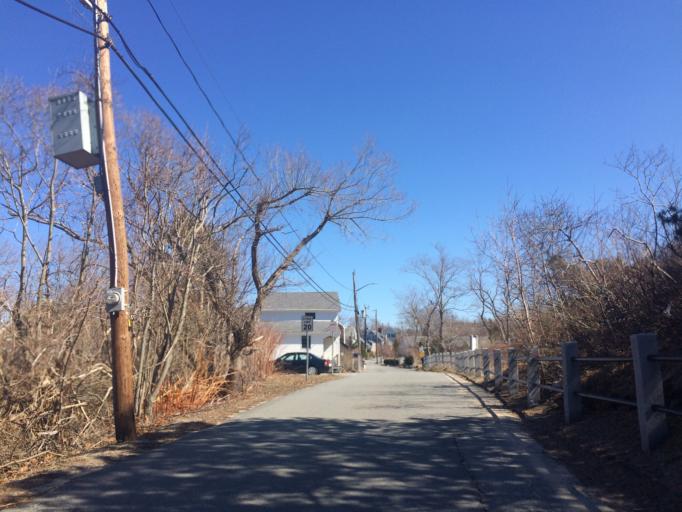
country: US
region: Massachusetts
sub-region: Barnstable County
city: Provincetown
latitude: 42.0503
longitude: -70.1931
